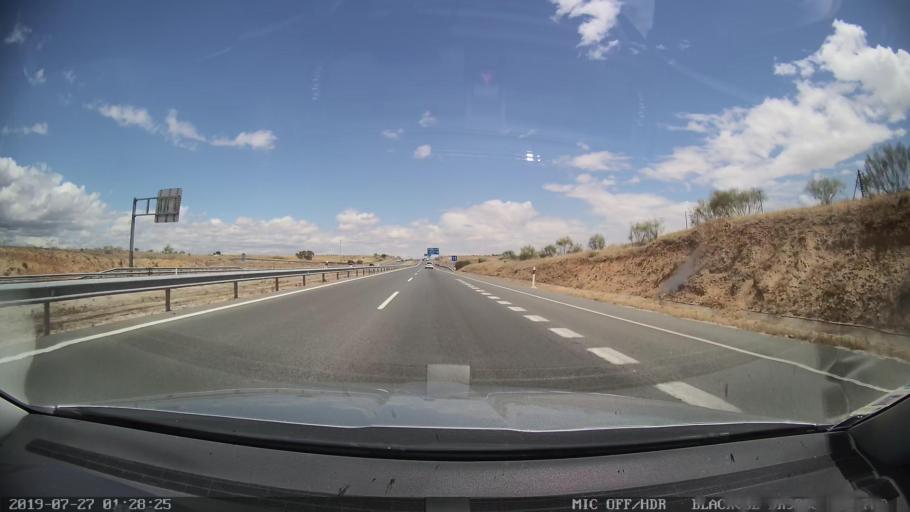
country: ES
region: Castille-La Mancha
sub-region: Province of Toledo
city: Las Ventas de Retamosa
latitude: 40.1798
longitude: -4.1443
